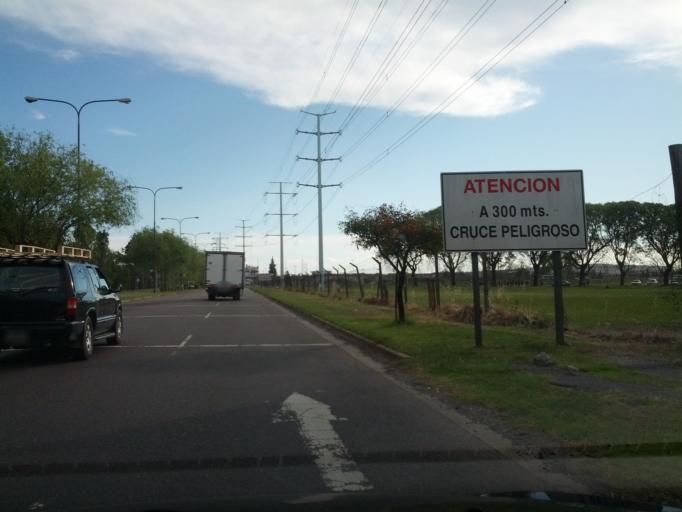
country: AR
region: Buenos Aires F.D.
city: Villa Lugano
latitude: -34.7016
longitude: -58.4587
